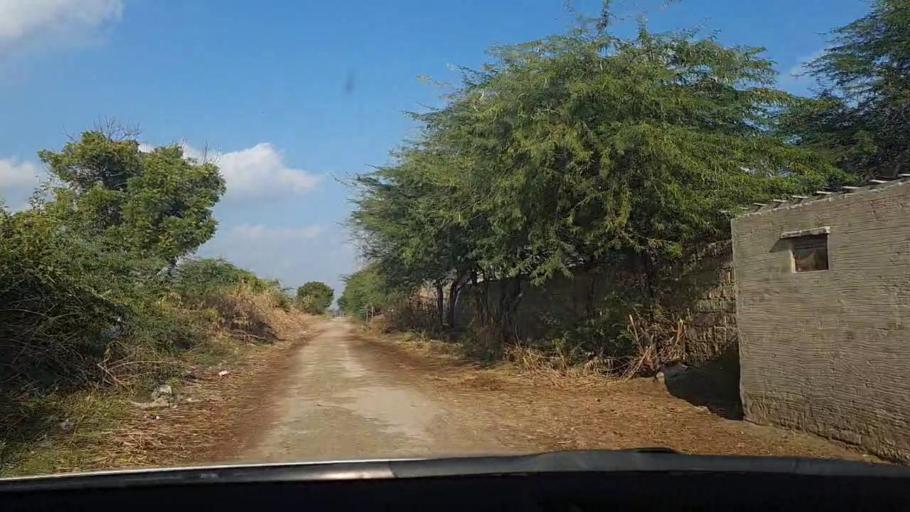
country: PK
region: Sindh
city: Tando Mittha Khan
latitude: 25.8850
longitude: 69.2974
